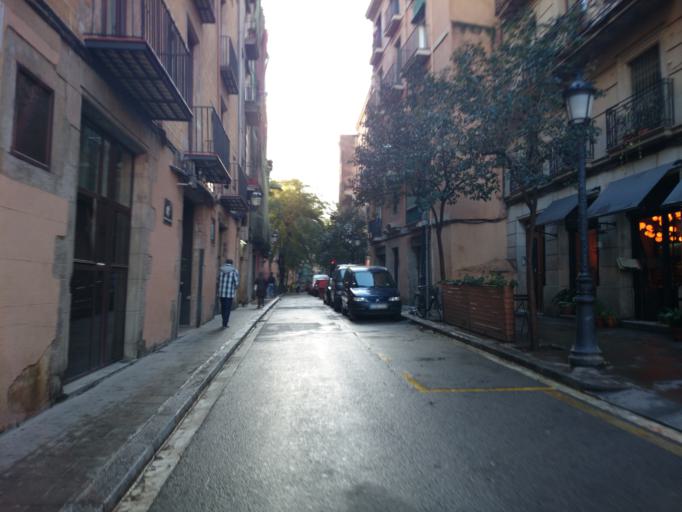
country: ES
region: Catalonia
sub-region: Provincia de Barcelona
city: Ciutat Vella
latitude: 41.3899
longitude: 2.1799
